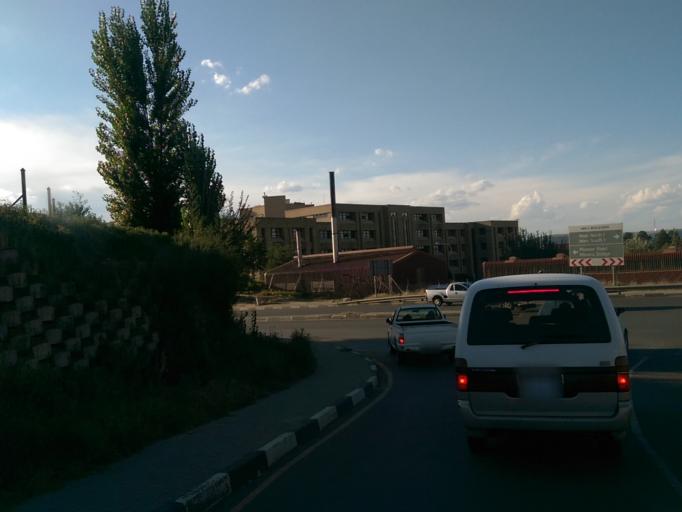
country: LS
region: Maseru
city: Maseru
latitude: -29.3173
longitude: 27.4863
